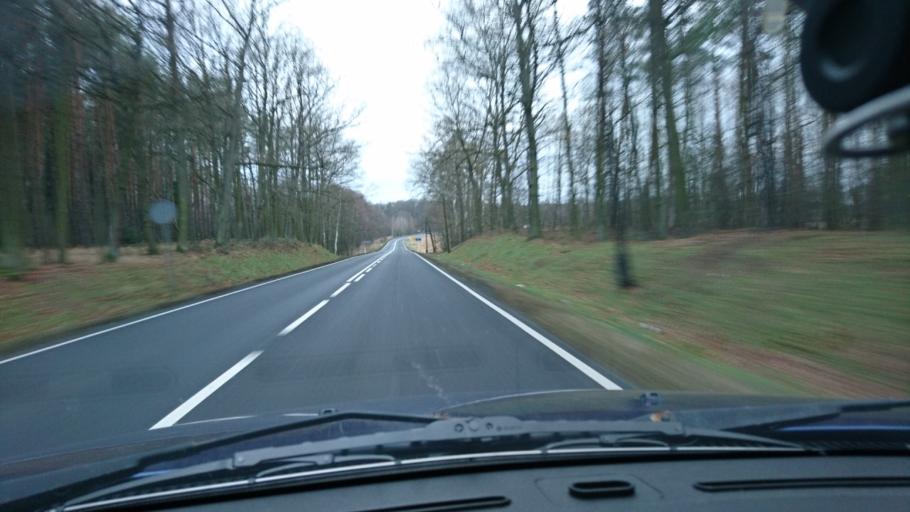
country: PL
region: Opole Voivodeship
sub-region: Powiat kluczborski
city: Kluczbork
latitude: 50.9516
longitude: 18.3115
